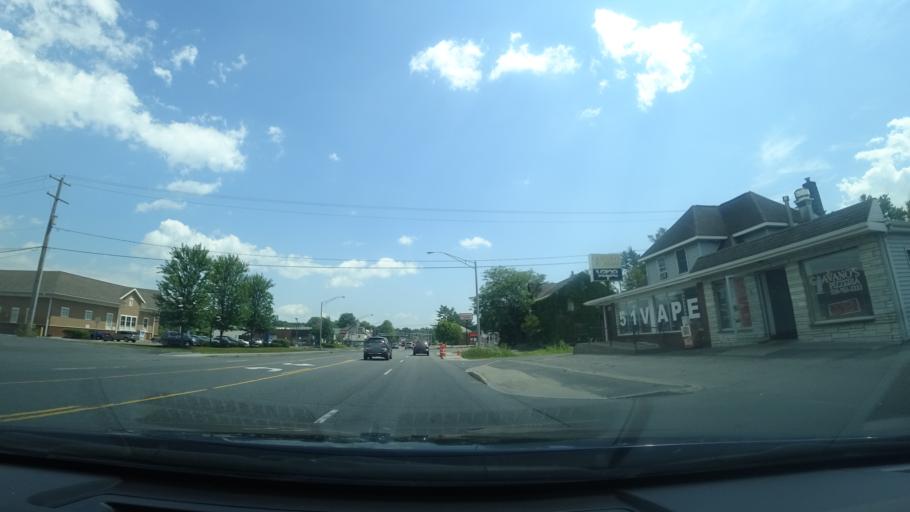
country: US
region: New York
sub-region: Warren County
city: Glens Falls North
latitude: 43.3281
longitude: -73.6689
